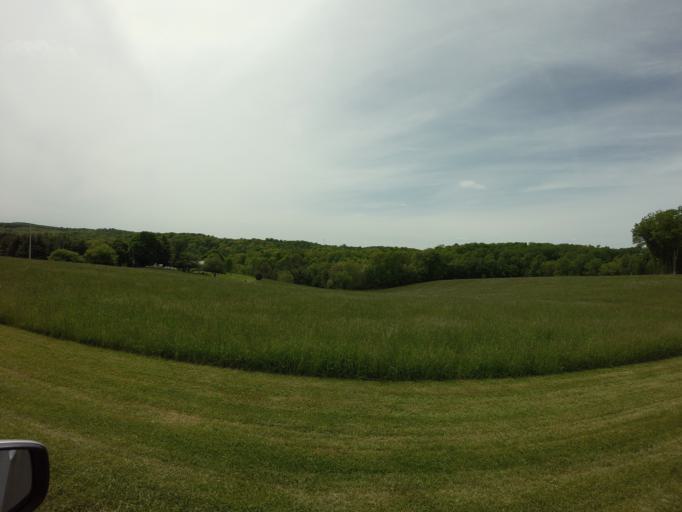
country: US
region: Maryland
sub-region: Carroll County
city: Eldersburg
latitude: 39.4787
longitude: -76.9761
